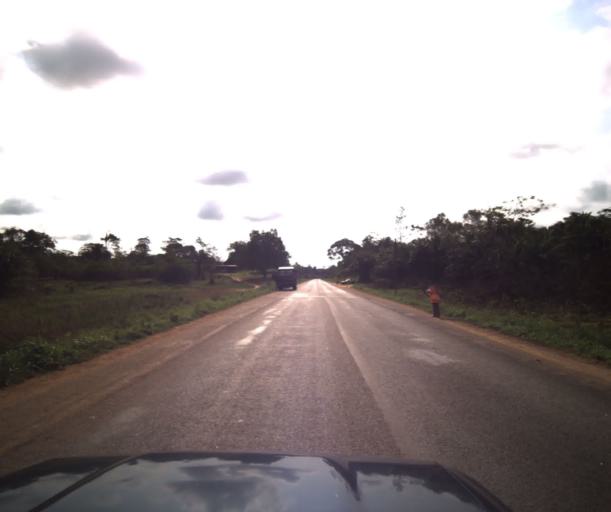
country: CM
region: Littoral
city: Edea
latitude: 3.9489
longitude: 10.0352
